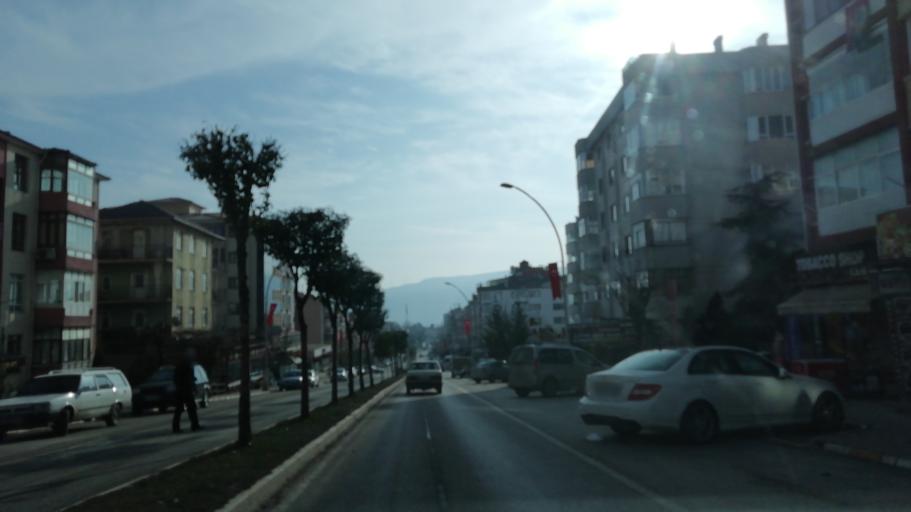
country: TR
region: Karabuk
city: Safranbolu
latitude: 41.2536
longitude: 32.6782
